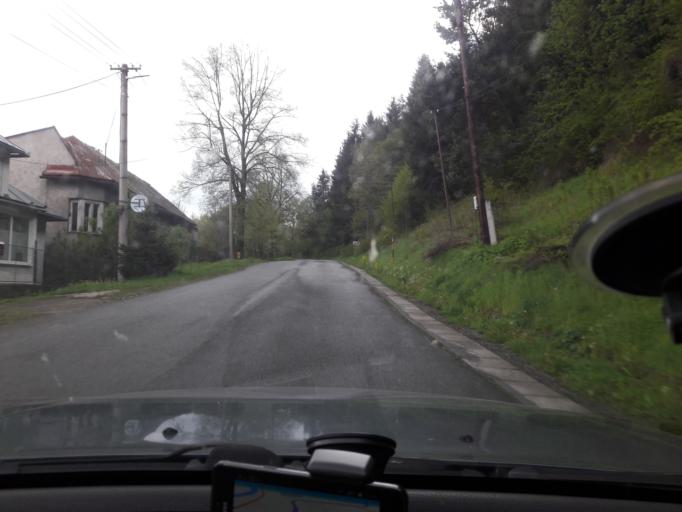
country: SK
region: Banskobystricky
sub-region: Okres Banska Bystrica
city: Brezno
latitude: 48.8149
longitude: 19.5714
